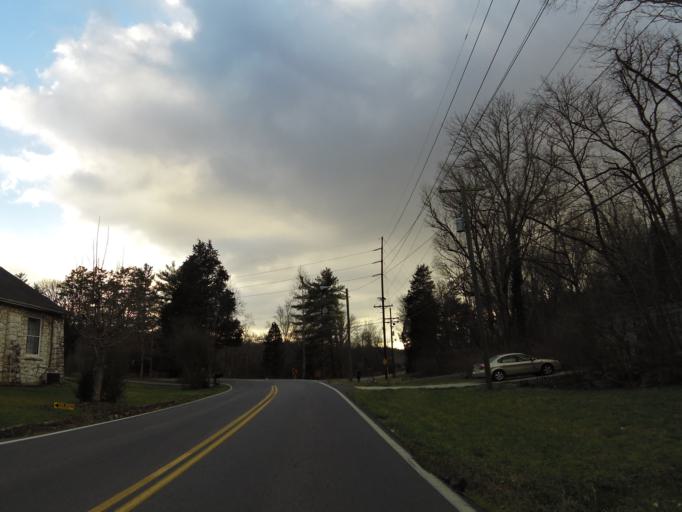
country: US
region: Tennessee
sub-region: Knox County
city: Knoxville
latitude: 35.9252
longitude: -83.8960
